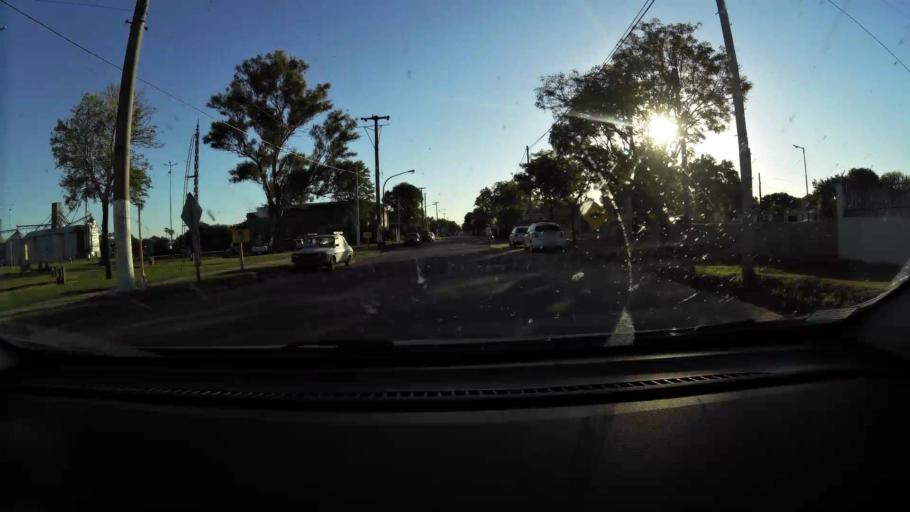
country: AR
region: Cordoba
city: Las Varillas
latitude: -31.8697
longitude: -62.7089
